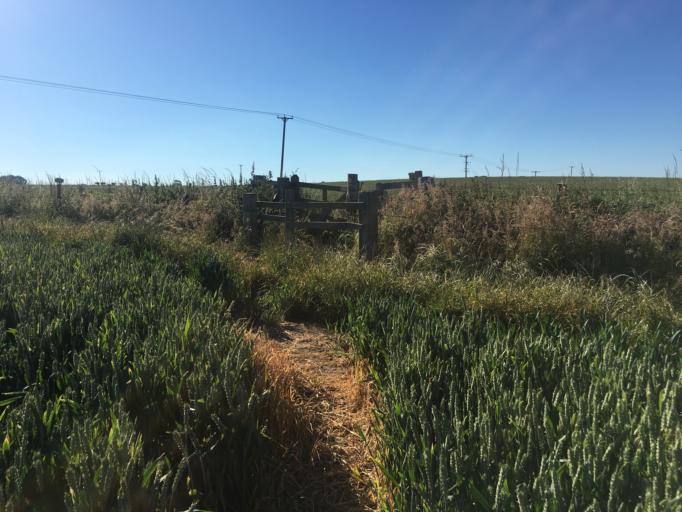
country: GB
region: England
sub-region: Northumberland
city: North Sunderland
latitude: 55.5689
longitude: -1.6567
